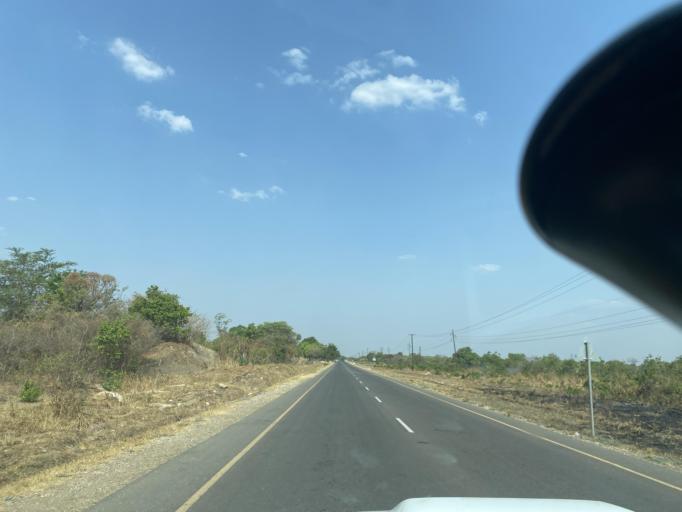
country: ZM
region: Lusaka
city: Lusaka
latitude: -15.3424
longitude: 28.0839
